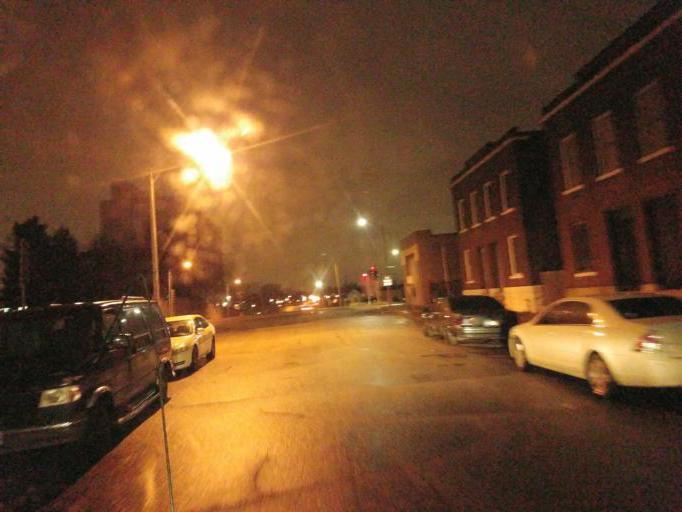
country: US
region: Missouri
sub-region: City of Saint Louis
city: St. Louis
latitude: 38.6561
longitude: -90.2026
